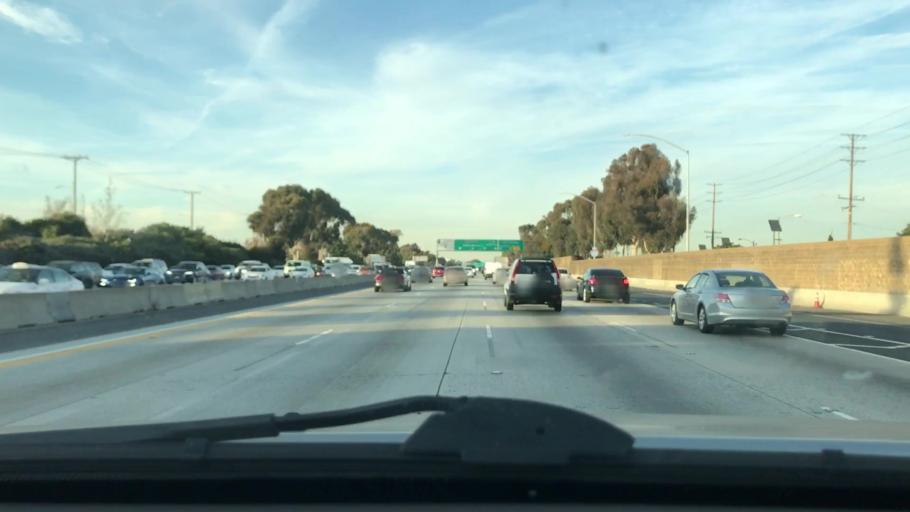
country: US
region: California
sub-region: Los Angeles County
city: Del Aire
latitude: 33.9047
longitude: -118.3703
